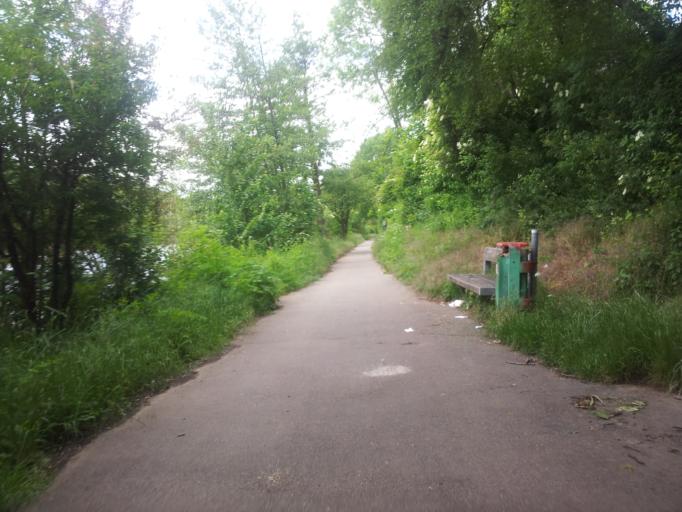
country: DE
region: Baden-Wuerttemberg
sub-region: Regierungsbezirk Stuttgart
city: Esslingen
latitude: 48.7393
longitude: 9.2954
